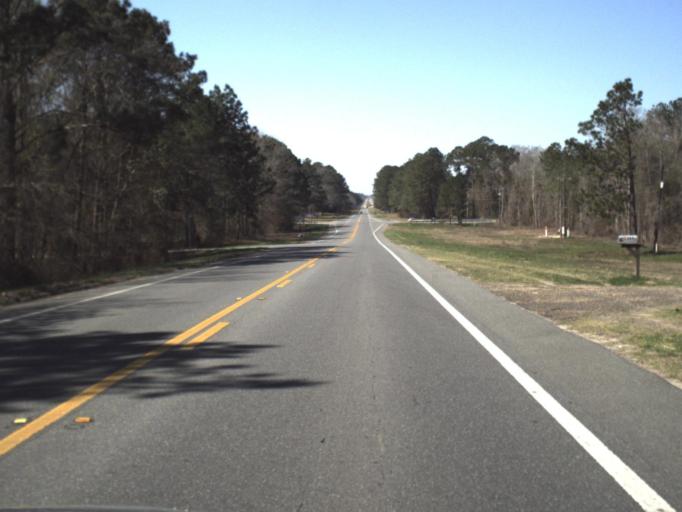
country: US
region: Florida
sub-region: Jackson County
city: Sneads
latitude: 30.7187
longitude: -84.9704
